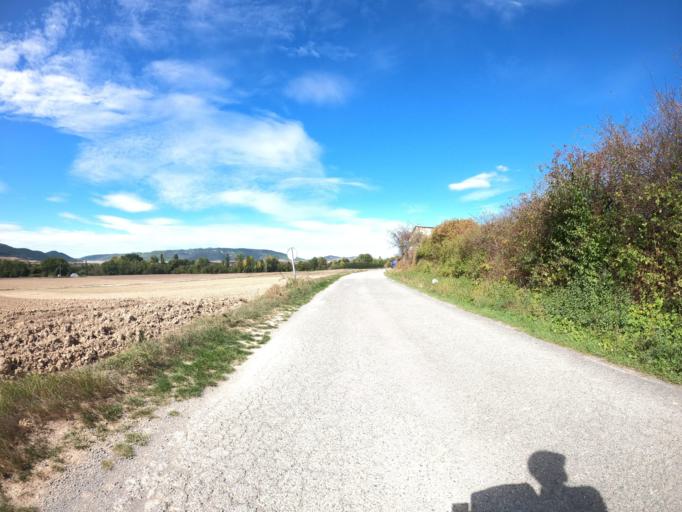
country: ES
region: Navarre
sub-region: Provincia de Navarra
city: Lumbier
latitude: 42.6400
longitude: -1.3096
